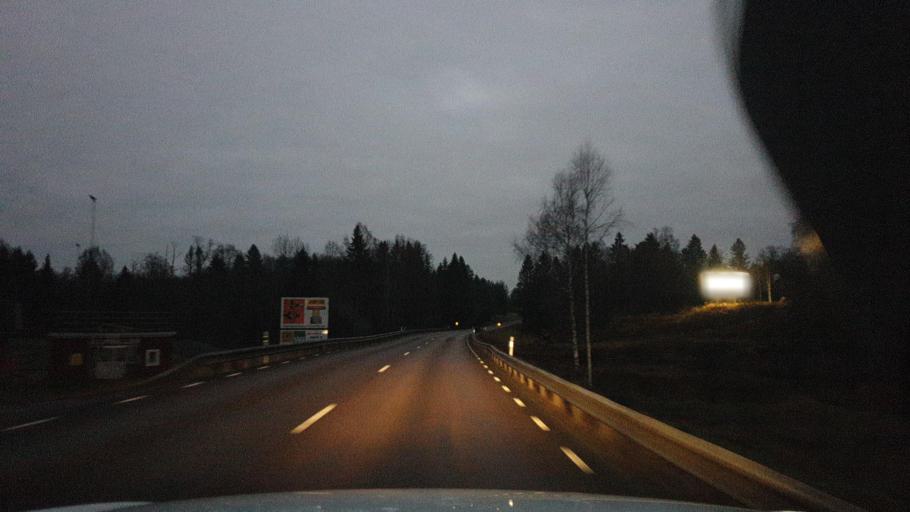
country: SE
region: Vaermland
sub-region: Eda Kommun
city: Charlottenberg
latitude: 59.9193
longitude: 12.2716
